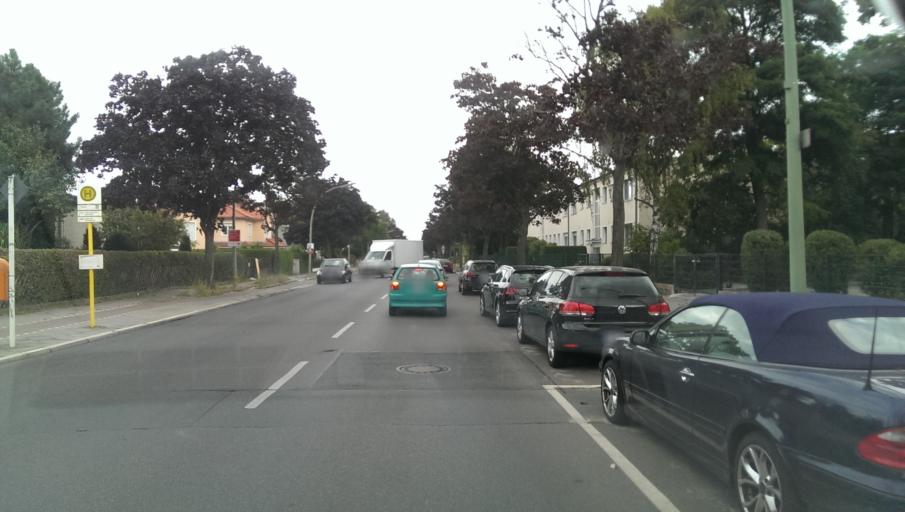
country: DE
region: Berlin
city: Lichtenrade
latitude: 52.4077
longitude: 13.4161
